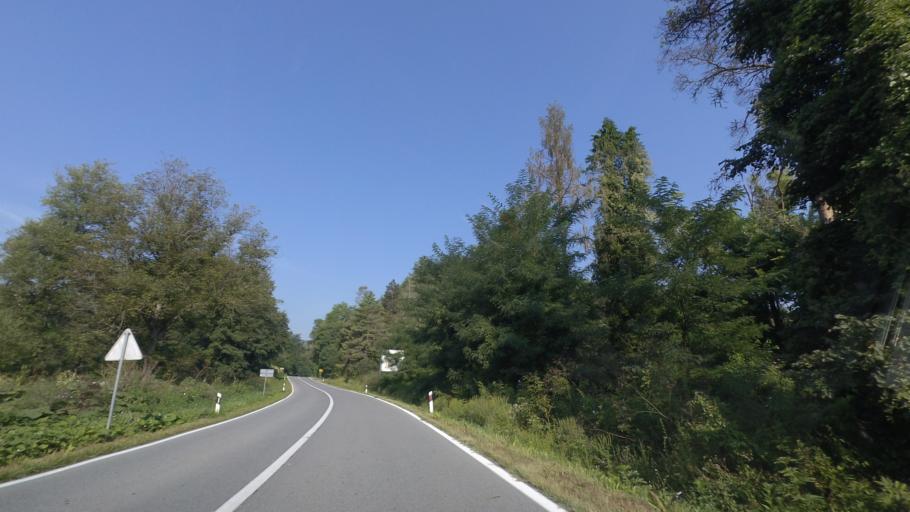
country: HR
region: Pozesko-Slavonska
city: Velika
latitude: 45.4441
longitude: 17.4795
